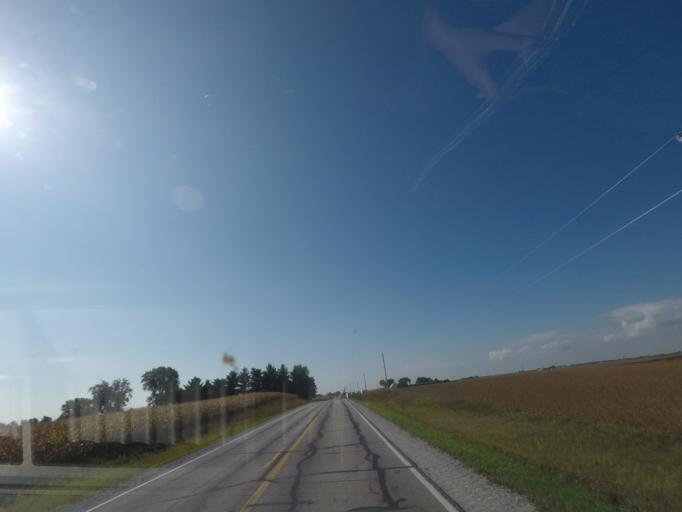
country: US
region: Iowa
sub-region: Story County
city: Nevada
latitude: 42.0279
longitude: -93.4059
